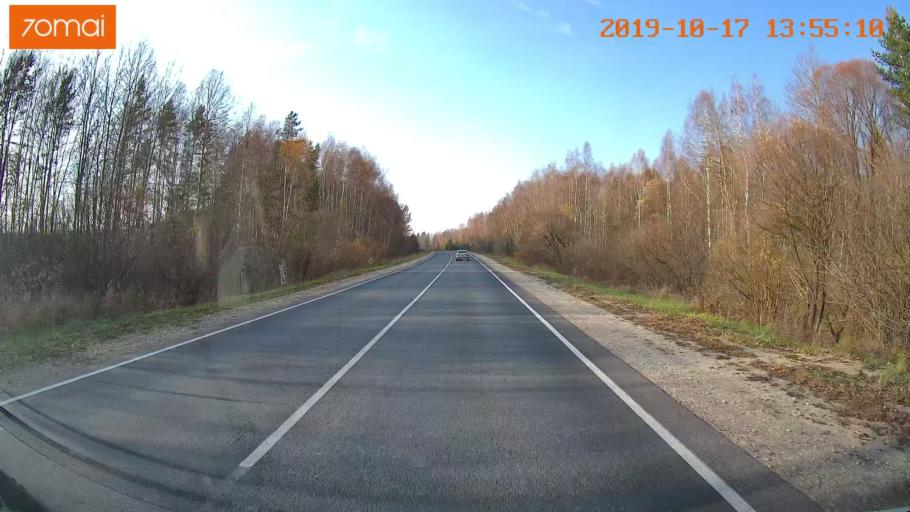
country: RU
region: Rjazan
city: Spas-Klepiki
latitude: 55.1507
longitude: 40.2962
